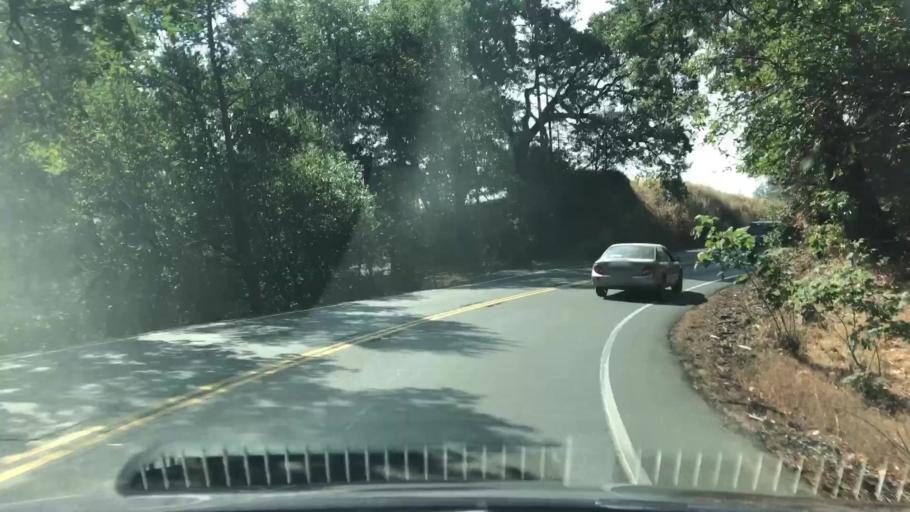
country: US
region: California
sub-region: Napa County
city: Calistoga
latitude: 38.6250
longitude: -122.5992
